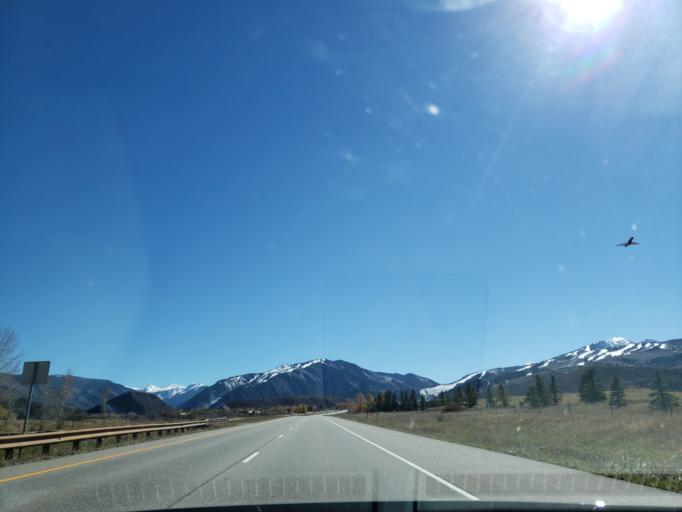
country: US
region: Colorado
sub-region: Pitkin County
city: Aspen
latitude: 39.2319
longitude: -106.8703
